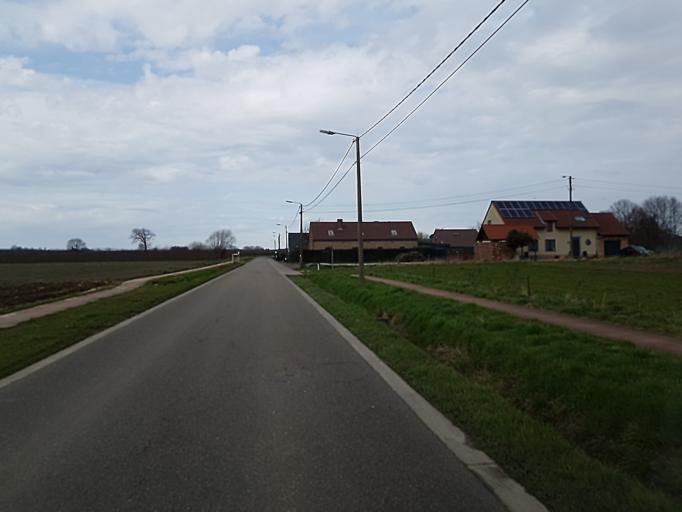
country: BE
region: Flanders
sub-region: Provincie Limburg
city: Nieuwerkerken
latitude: 50.8614
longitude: 5.2376
